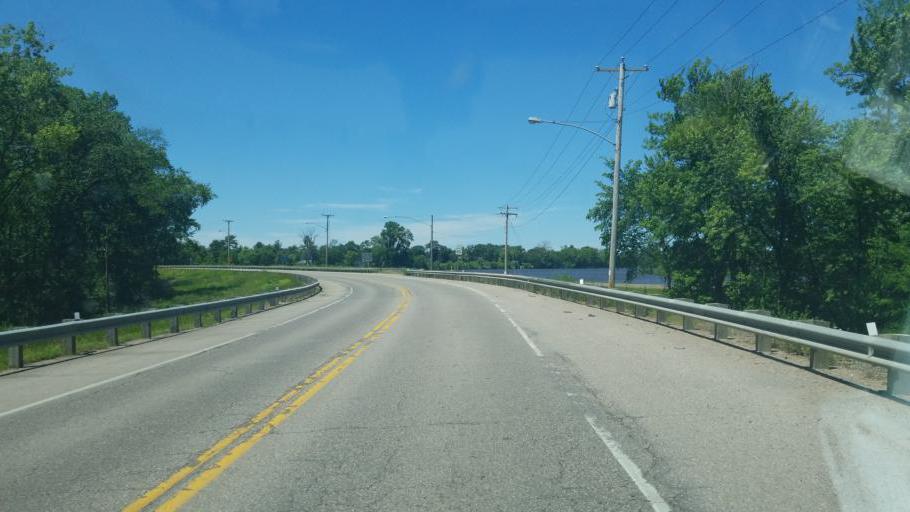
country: US
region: Wisconsin
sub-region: Juneau County
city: New Lisbon
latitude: 44.0278
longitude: -90.0686
